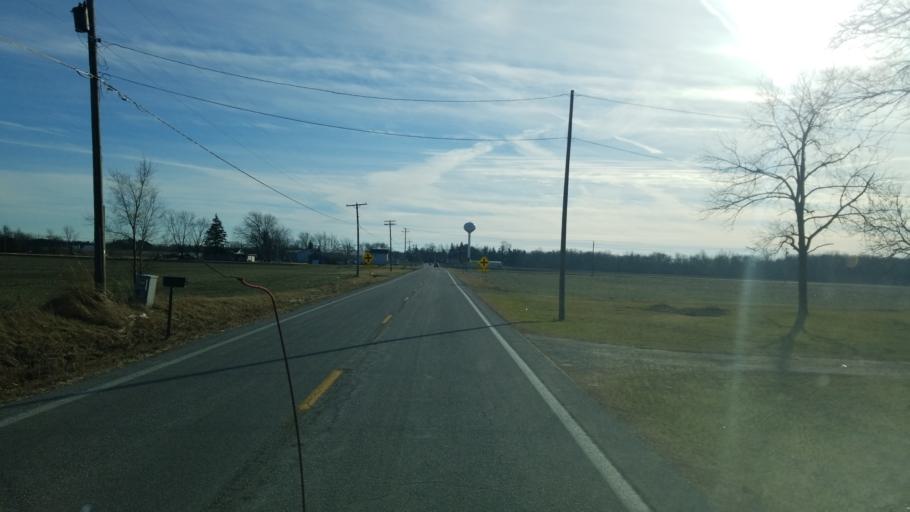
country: US
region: Ohio
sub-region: Sandusky County
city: Green Springs
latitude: 41.2733
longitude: -83.0525
